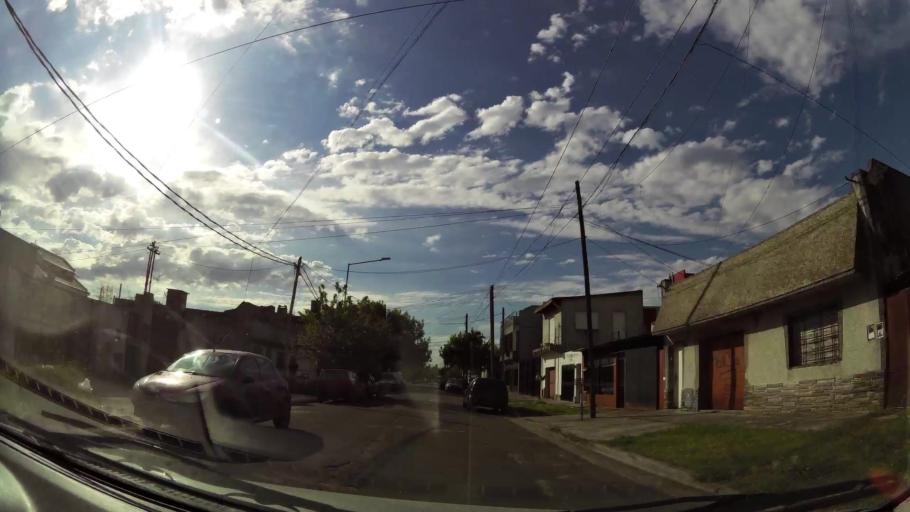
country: AR
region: Buenos Aires
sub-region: Partido de Lanus
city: Lanus
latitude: -34.6915
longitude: -58.3753
